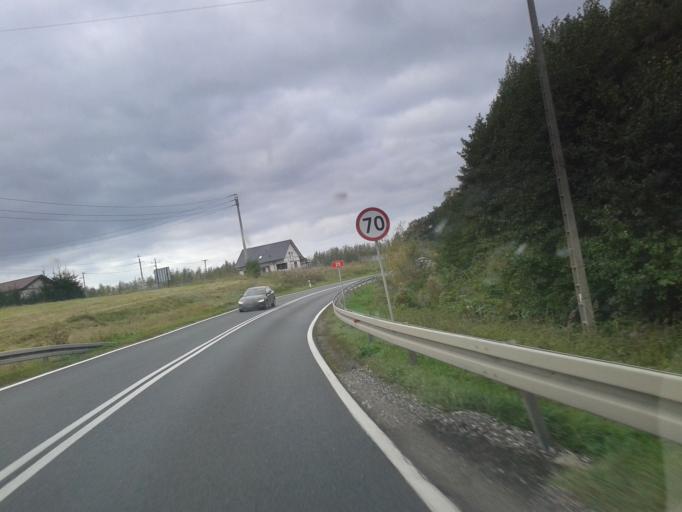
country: PL
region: Kujawsko-Pomorskie
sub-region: Powiat sepolenski
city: Sepolno Krajenskie
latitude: 53.4674
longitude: 17.5280
